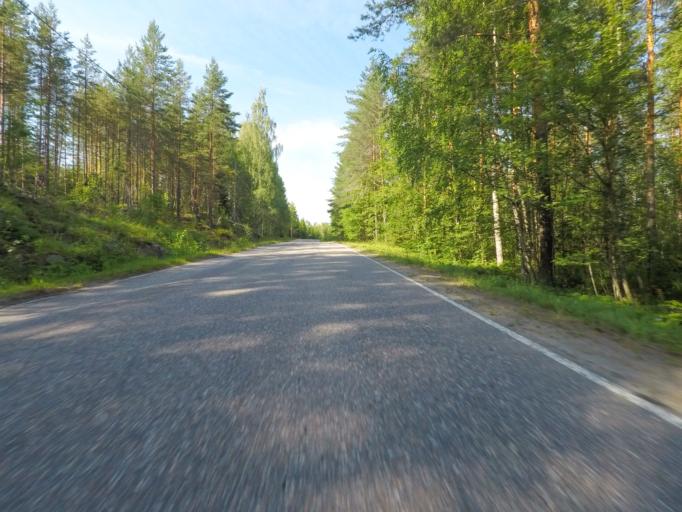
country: FI
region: Southern Savonia
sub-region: Mikkeli
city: Puumala
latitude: 61.6111
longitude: 28.2206
